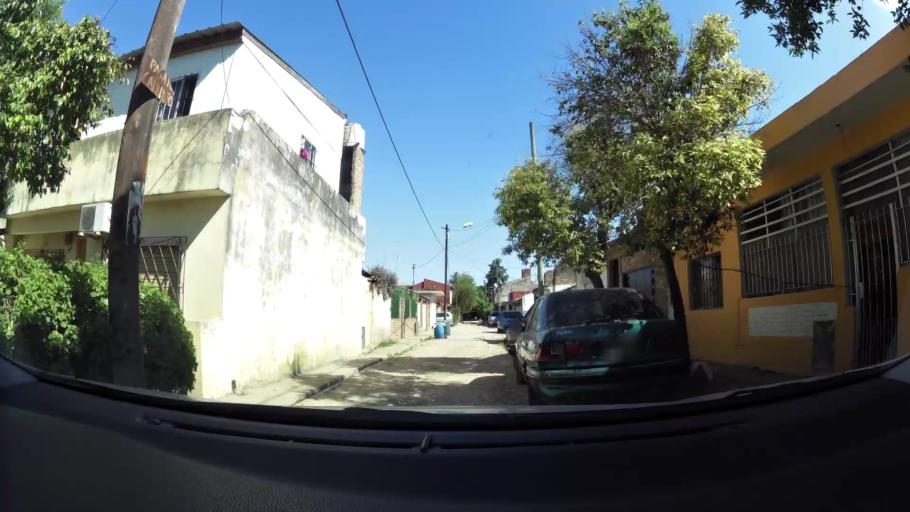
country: AR
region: Buenos Aires F.D.
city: Villa Lugano
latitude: -34.7070
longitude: -58.4769
